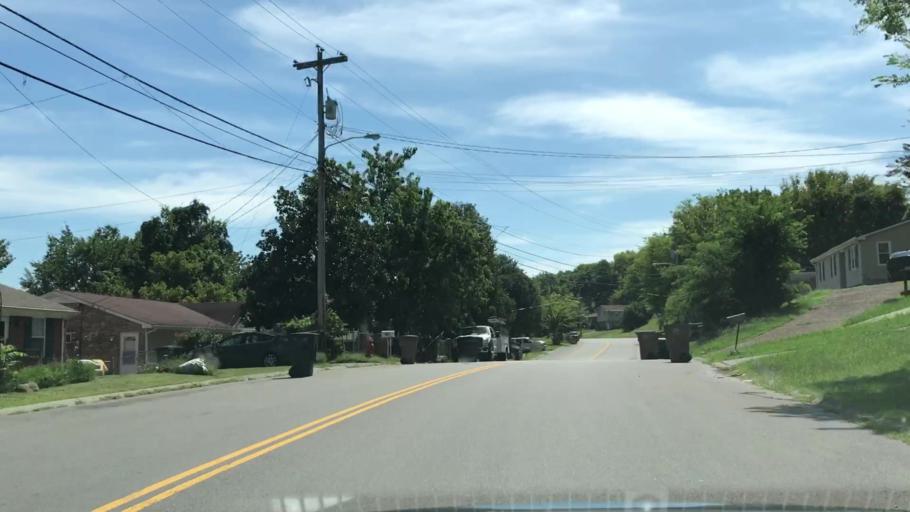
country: US
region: Tennessee
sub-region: Williamson County
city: Brentwood Estates
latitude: 36.0357
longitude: -86.7064
